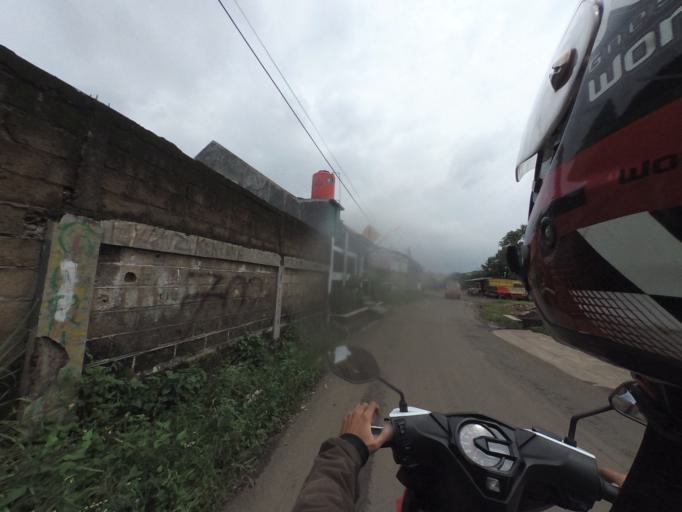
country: ID
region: West Java
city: Bogor
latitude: -6.6071
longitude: 106.7583
